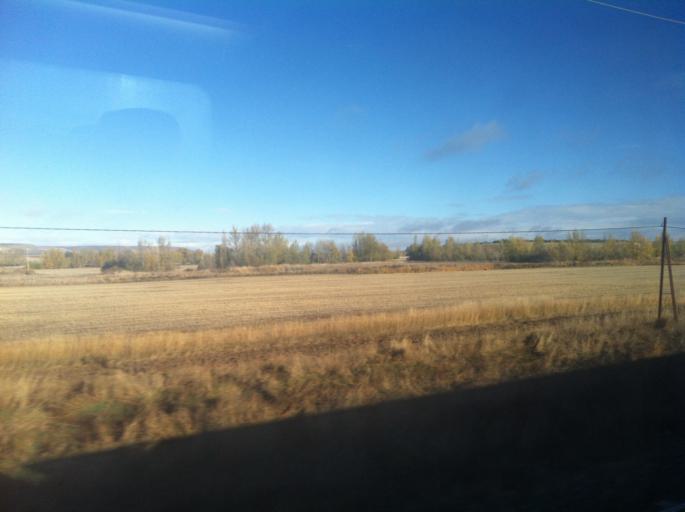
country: ES
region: Castille and Leon
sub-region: Provincia de Burgos
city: Celada del Camino
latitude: 42.2637
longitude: -3.9160
